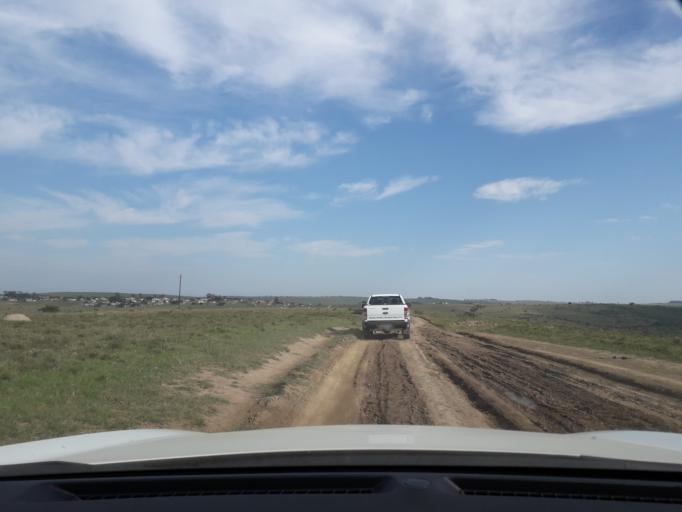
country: ZA
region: Eastern Cape
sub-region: Buffalo City Metropolitan Municipality
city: Bhisho
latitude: -32.9928
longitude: 27.3479
